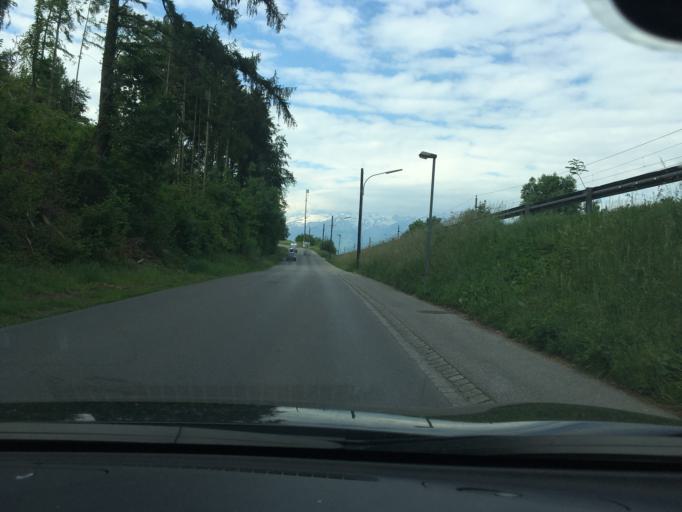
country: AT
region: Vorarlberg
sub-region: Politischer Bezirk Feldkirch
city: Nofels
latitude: 47.2347
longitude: 9.5797
